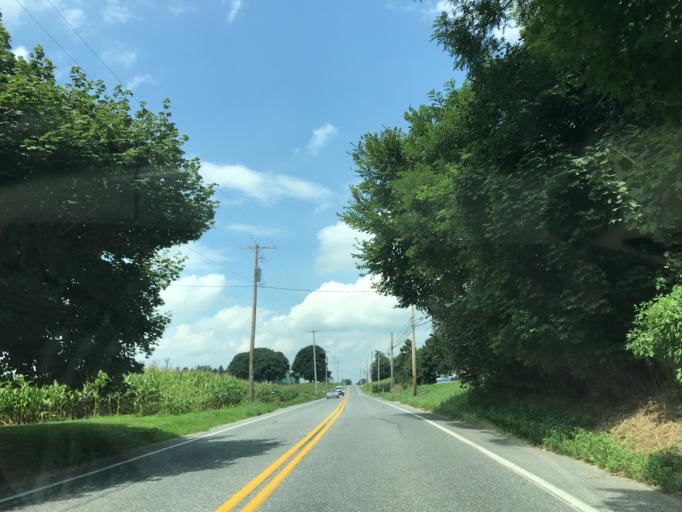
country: US
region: Pennsylvania
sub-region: York County
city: Red Lion
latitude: 39.8519
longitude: -76.6206
